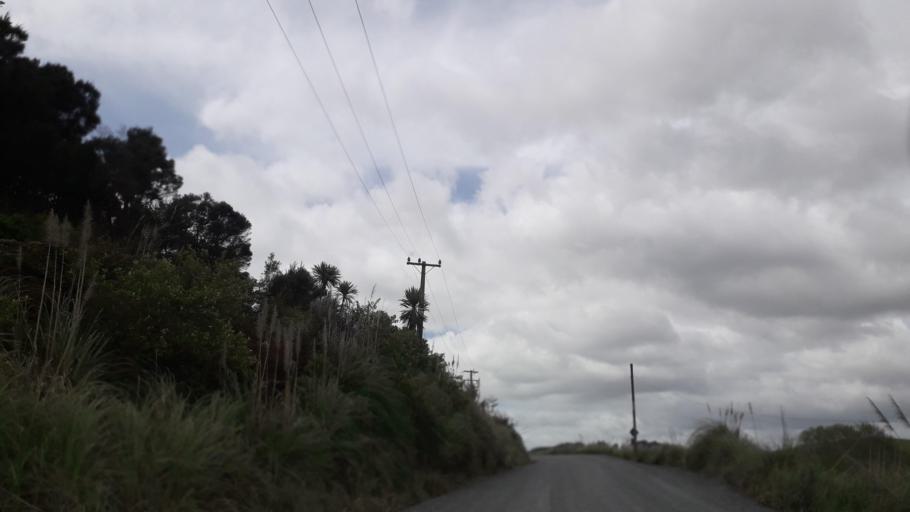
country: NZ
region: Northland
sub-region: Far North District
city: Taipa
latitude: -35.0086
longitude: 173.4283
